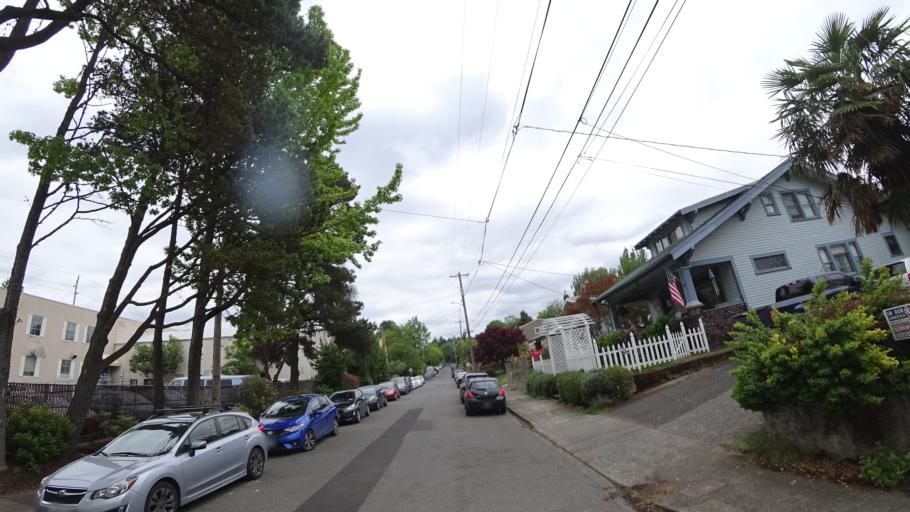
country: US
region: Oregon
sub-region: Multnomah County
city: Lents
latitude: 45.5159
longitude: -122.6153
